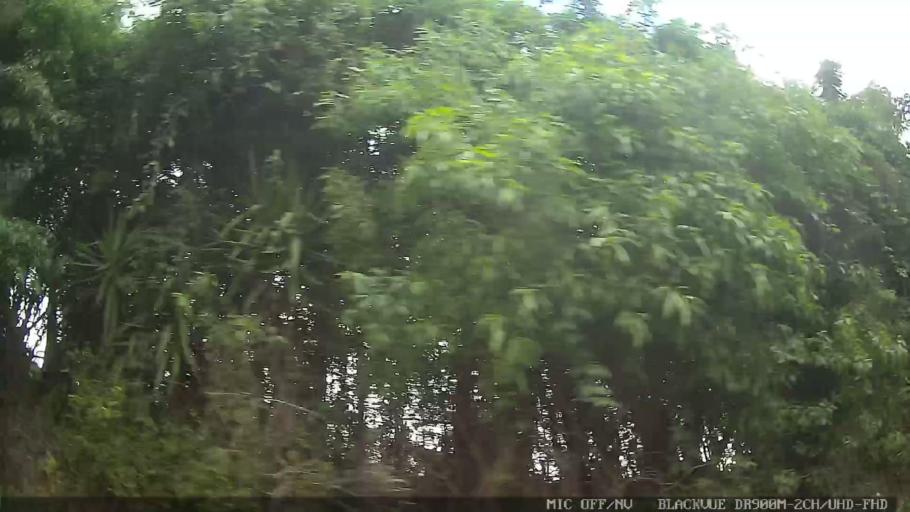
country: BR
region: Sao Paulo
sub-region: Jaguariuna
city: Jaguariuna
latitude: -22.6522
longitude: -47.0674
